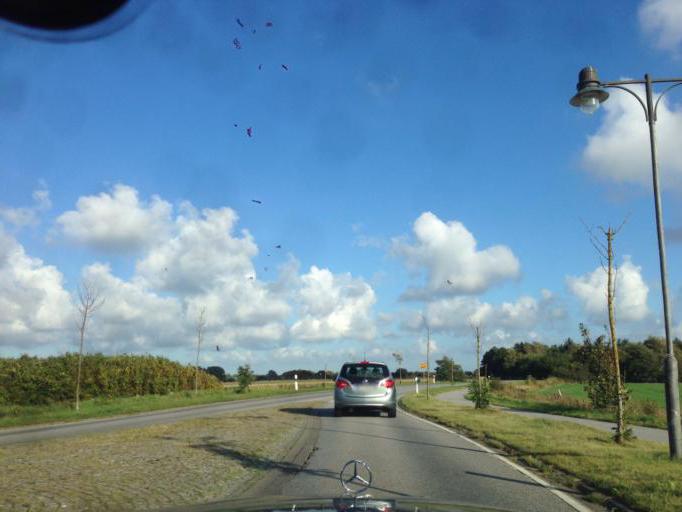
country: DE
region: Schleswig-Holstein
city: Sylt-Ost
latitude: 54.8728
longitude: 8.4007
